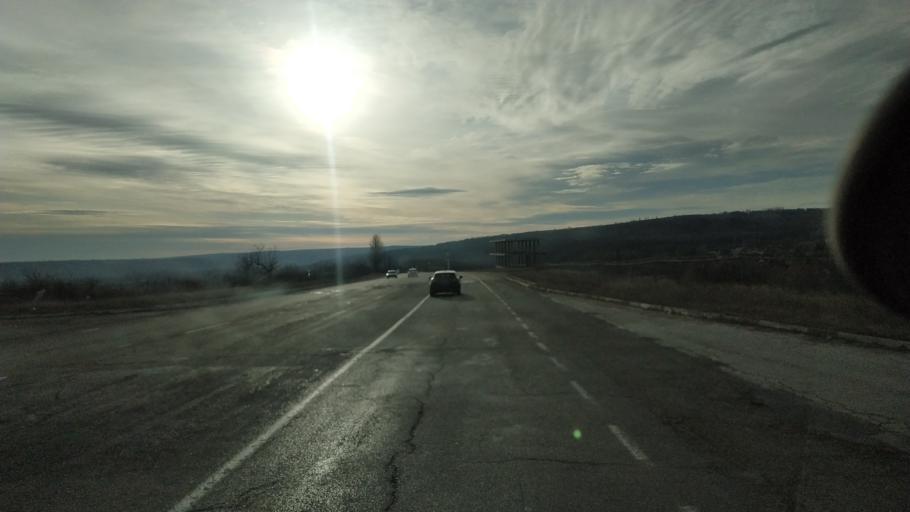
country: MD
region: Chisinau
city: Vadul lui Voda
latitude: 47.0874
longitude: 29.0724
